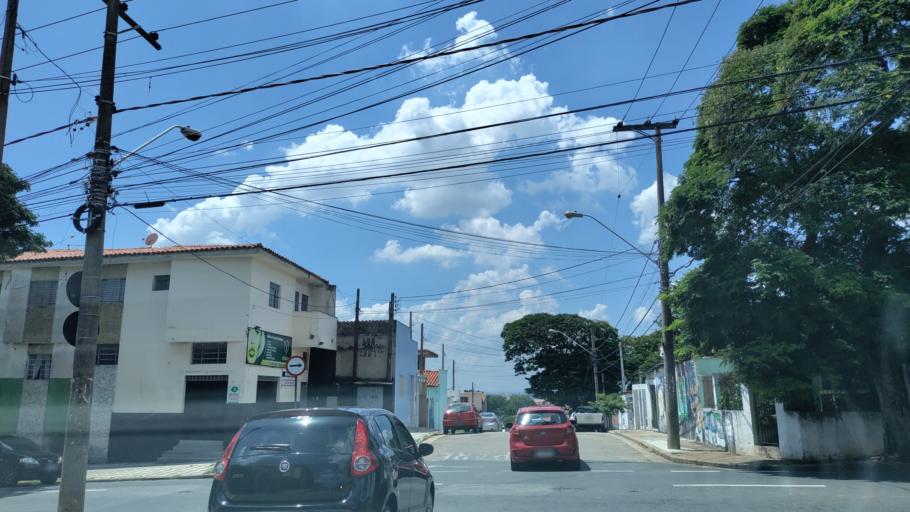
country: BR
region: Sao Paulo
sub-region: Sorocaba
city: Sorocaba
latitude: -23.4819
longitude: -47.4686
